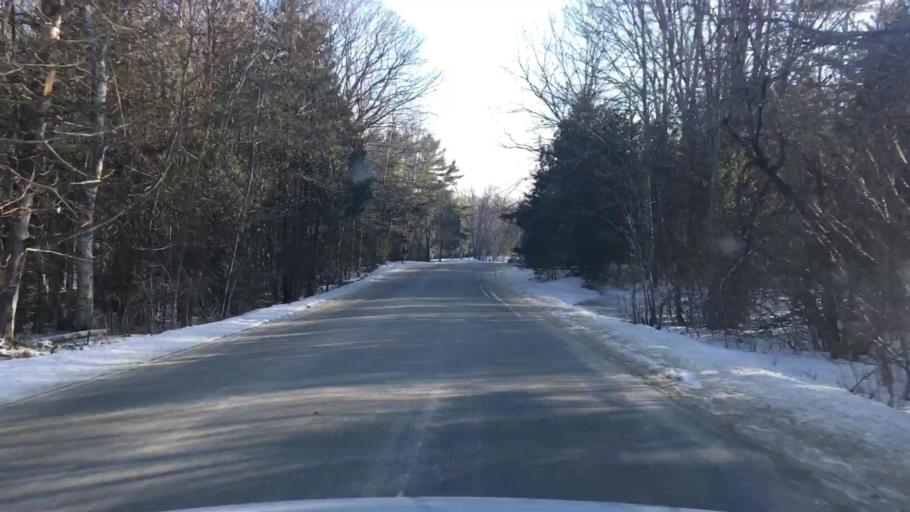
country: US
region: Maine
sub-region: Hancock County
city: Castine
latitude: 44.3439
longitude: -68.7830
